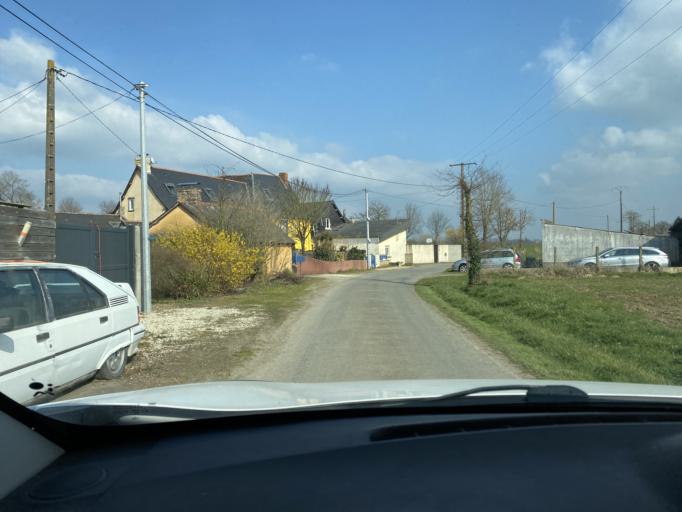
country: FR
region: Brittany
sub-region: Departement d'Ille-et-Vilaine
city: Saint-Medard-sur-Ille
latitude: 48.2397
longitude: -1.6645
